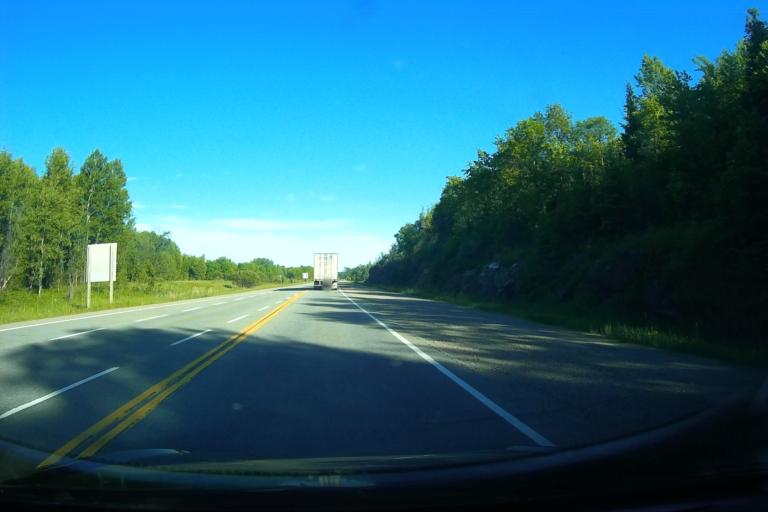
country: CA
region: Ontario
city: Renfrew
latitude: 45.5300
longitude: -76.6963
